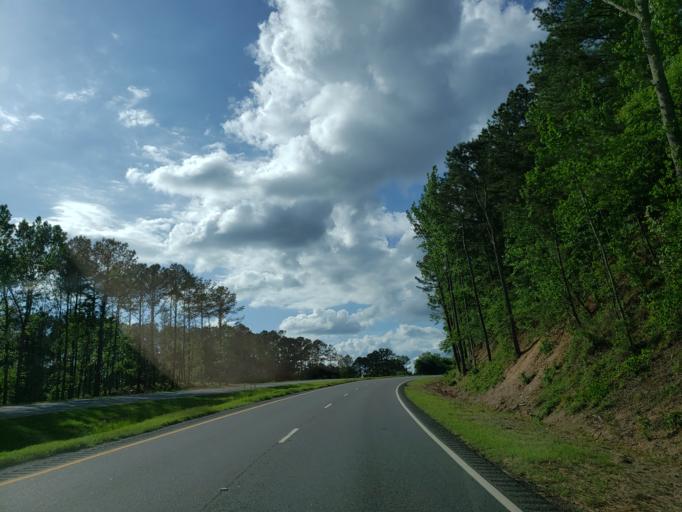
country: US
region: Georgia
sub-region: Bartow County
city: Cartersville
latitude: 34.2219
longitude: -84.8518
